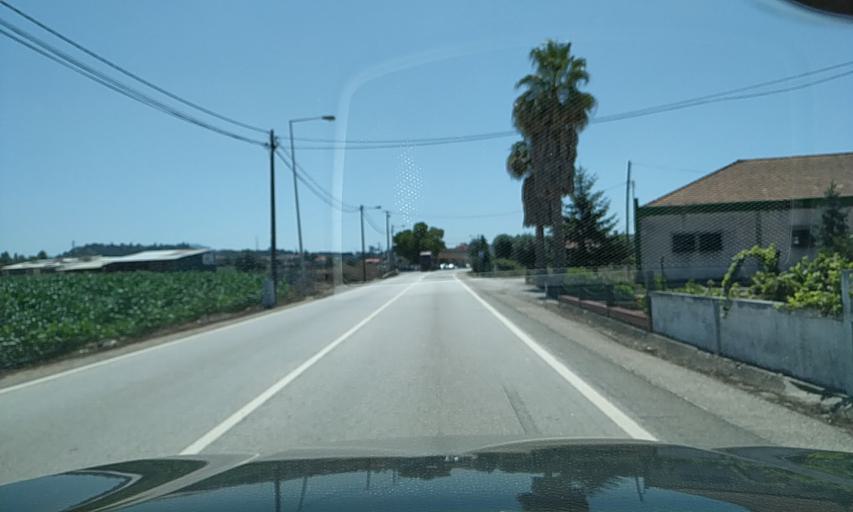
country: PT
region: Aveiro
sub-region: Anadia
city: Arcos
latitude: 40.4574
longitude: -8.4548
